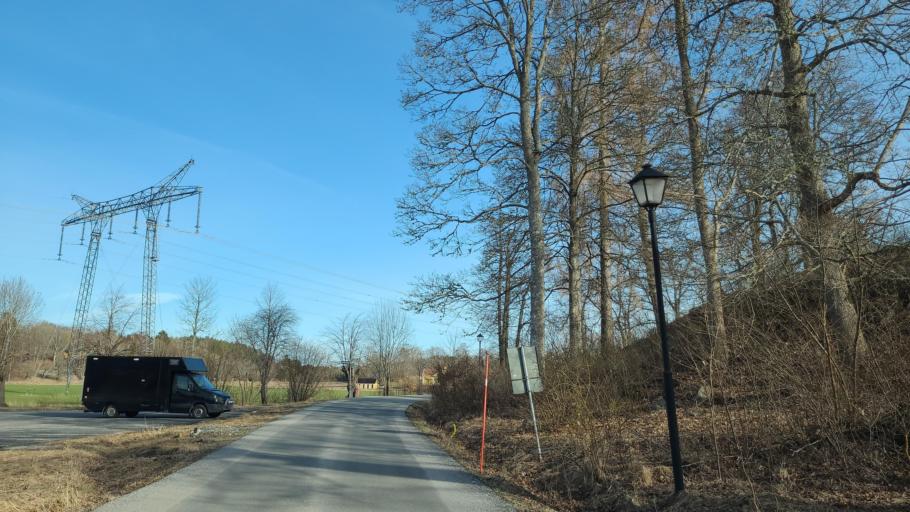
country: SE
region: Stockholm
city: Stenhamra
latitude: 59.2840
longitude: 17.6634
